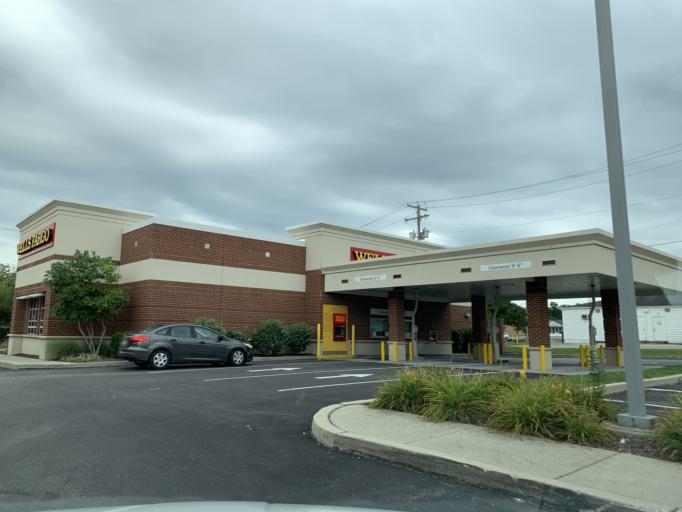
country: US
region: Pennsylvania
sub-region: York County
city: East York
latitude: 39.9732
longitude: -76.6805
